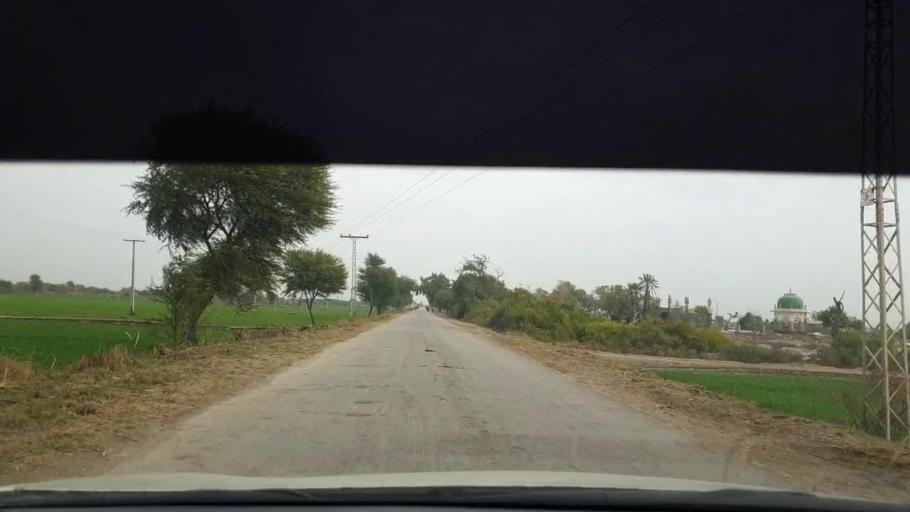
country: PK
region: Sindh
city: Berani
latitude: 25.7773
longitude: 68.9009
